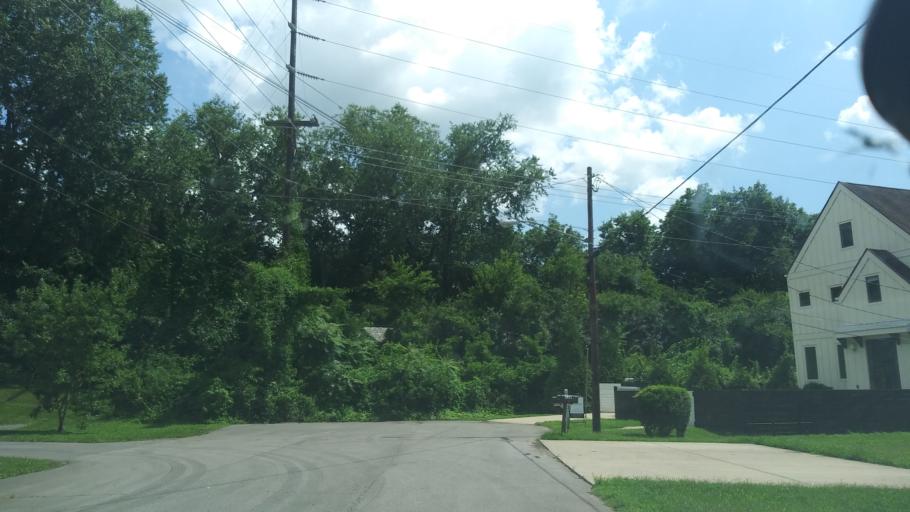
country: US
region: Tennessee
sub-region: Davidson County
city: Belle Meade
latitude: 36.1382
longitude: -86.8378
